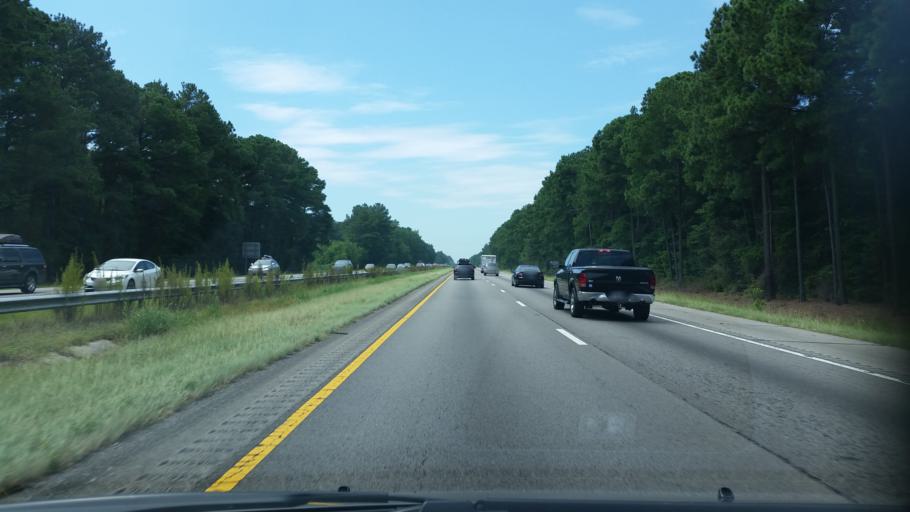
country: US
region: North Carolina
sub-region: Cumberland County
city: Eastover
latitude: 35.1527
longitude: -78.7232
